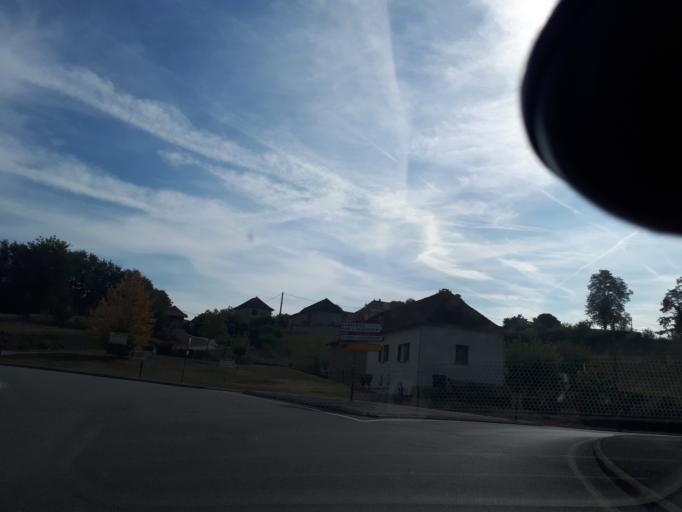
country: FR
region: Rhone-Alpes
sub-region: Departement de l'Isere
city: Aoste
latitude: 45.5741
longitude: 5.6124
